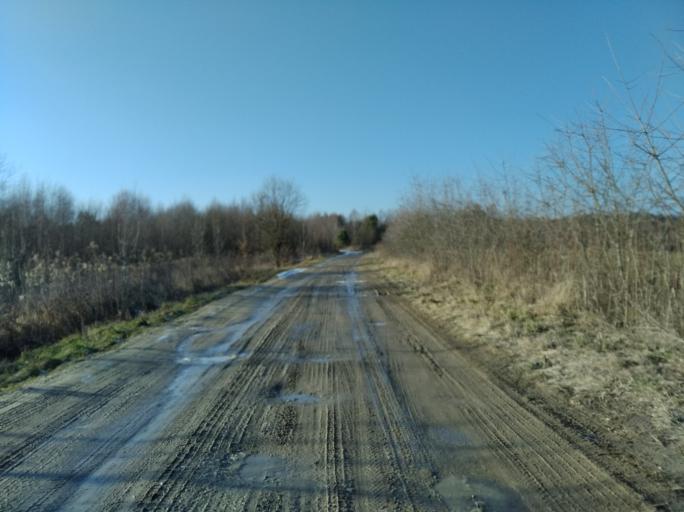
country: PL
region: Subcarpathian Voivodeship
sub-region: Powiat strzyzowski
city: Jawornik
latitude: 49.8302
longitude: 21.8681
